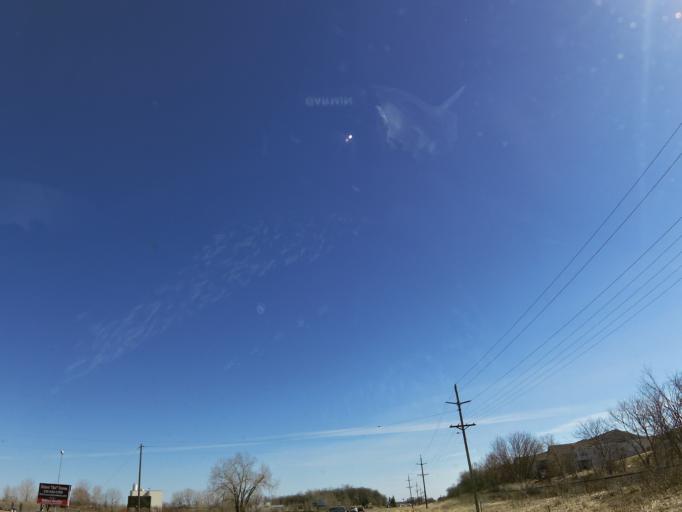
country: US
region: Minnesota
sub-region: Wright County
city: Buffalo
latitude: 45.1899
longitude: -93.8877
